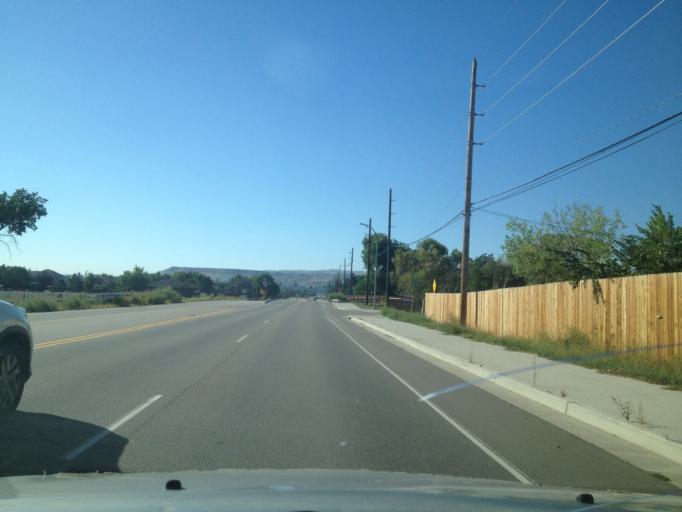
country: US
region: Colorado
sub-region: Jefferson County
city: Applewood
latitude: 39.7931
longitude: -105.1746
